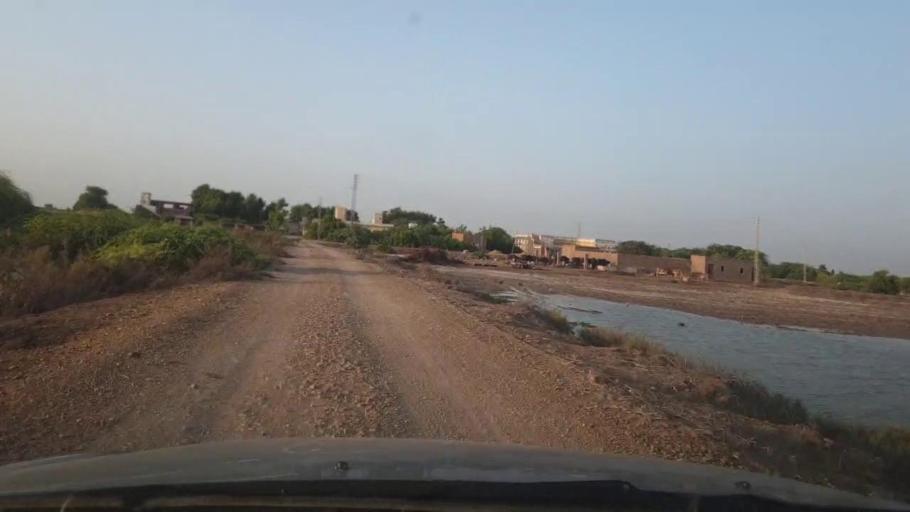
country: PK
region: Sindh
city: Tando Ghulam Ali
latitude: 25.1734
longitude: 68.9748
